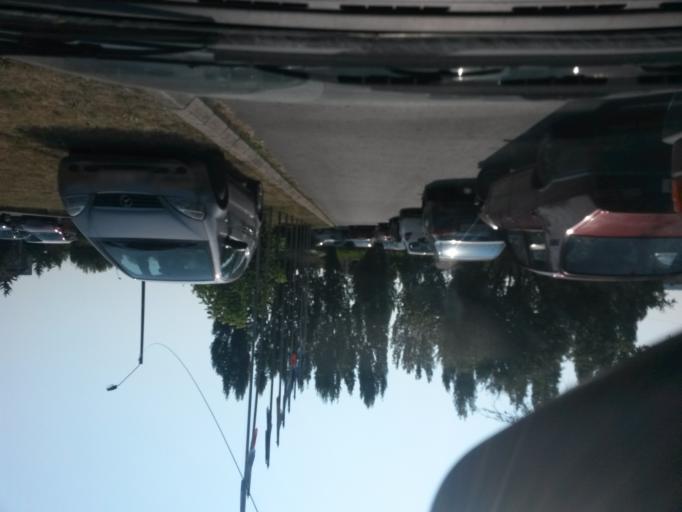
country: RO
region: Mures
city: Targu-Mures
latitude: 46.5502
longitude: 24.5523
